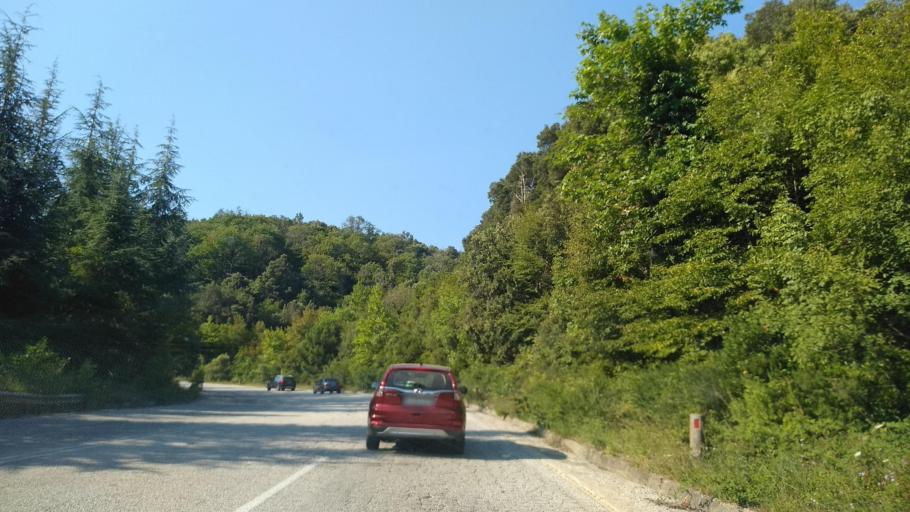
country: GR
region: Central Macedonia
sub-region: Nomos Chalkidikis
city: Stratonion
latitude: 40.5351
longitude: 23.8277
